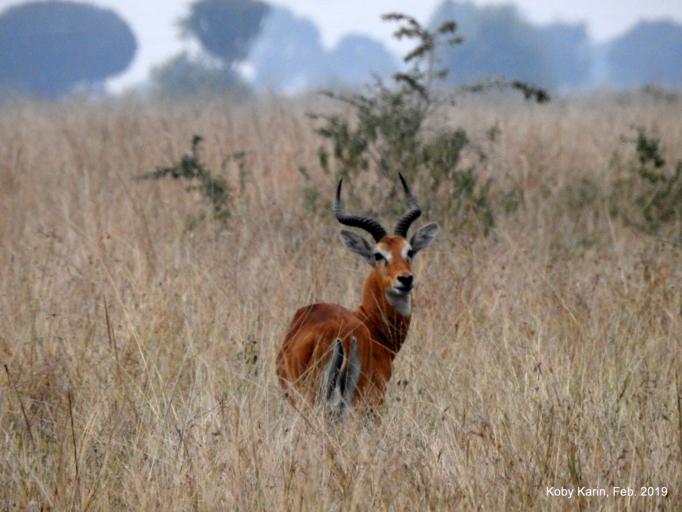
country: UG
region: Western Region
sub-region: Rubirizi District
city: Rubirizi
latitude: -0.0843
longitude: 30.0257
